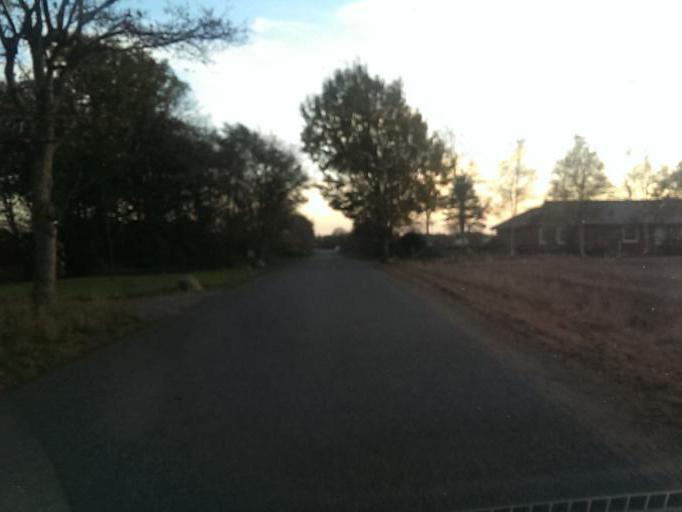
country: DK
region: South Denmark
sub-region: Esbjerg Kommune
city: Tjaereborg
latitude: 55.4725
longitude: 8.6154
